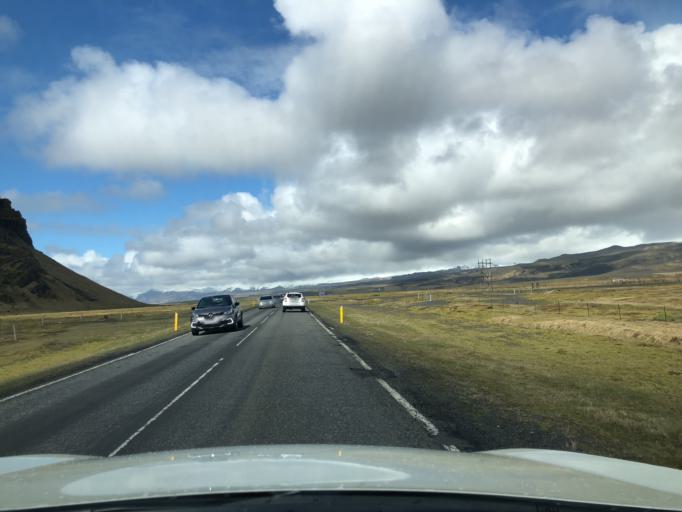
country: IS
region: South
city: Vestmannaeyjar
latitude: 63.4696
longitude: -19.2494
